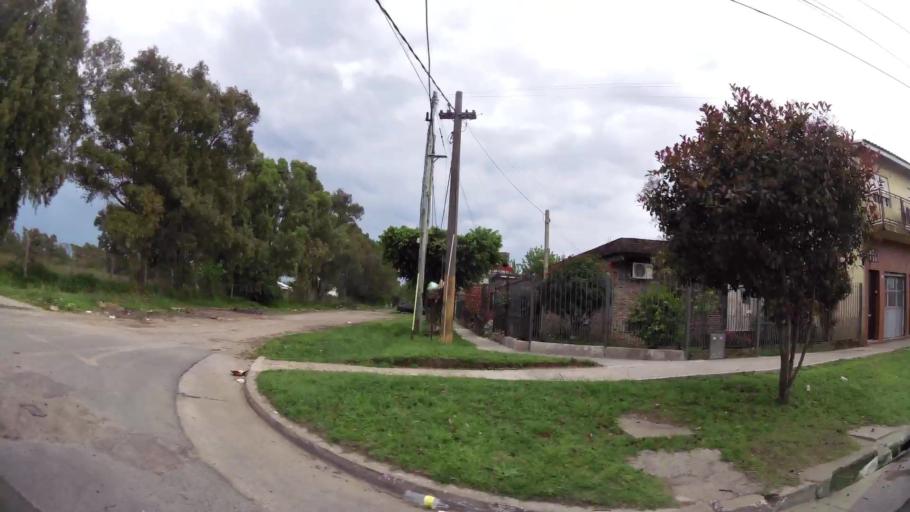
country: AR
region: Buenos Aires
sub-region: Partido de Quilmes
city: Quilmes
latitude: -34.7467
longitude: -58.2898
